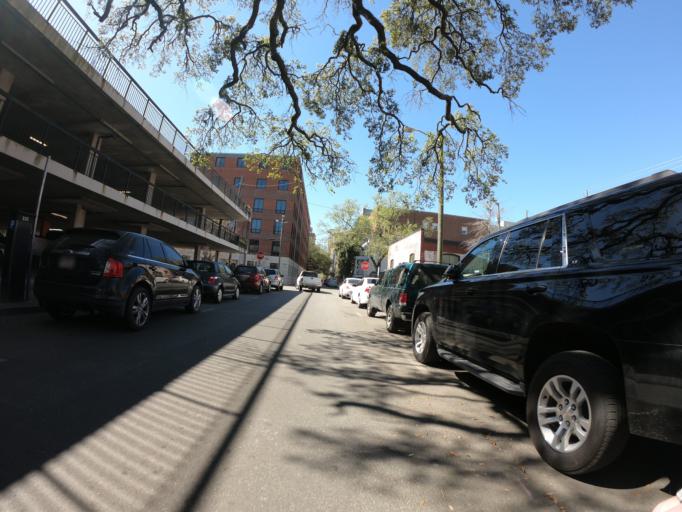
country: US
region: Georgia
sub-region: Chatham County
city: Savannah
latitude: 32.0792
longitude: -81.0877
